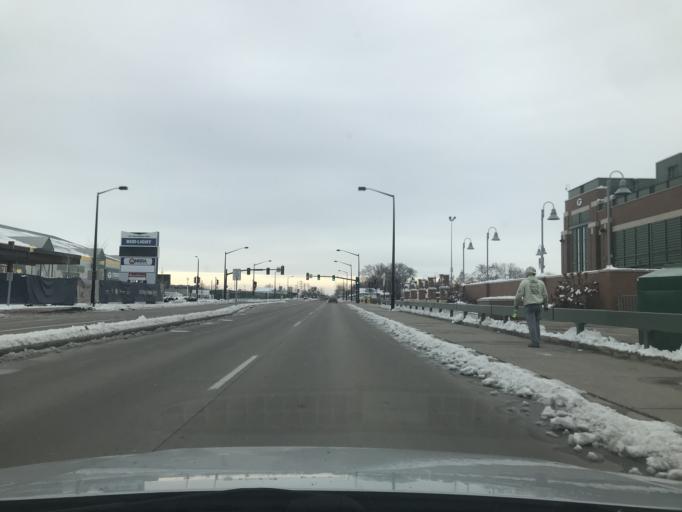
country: US
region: Wisconsin
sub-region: Brown County
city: Ashwaubenon
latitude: 44.5006
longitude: -88.0577
